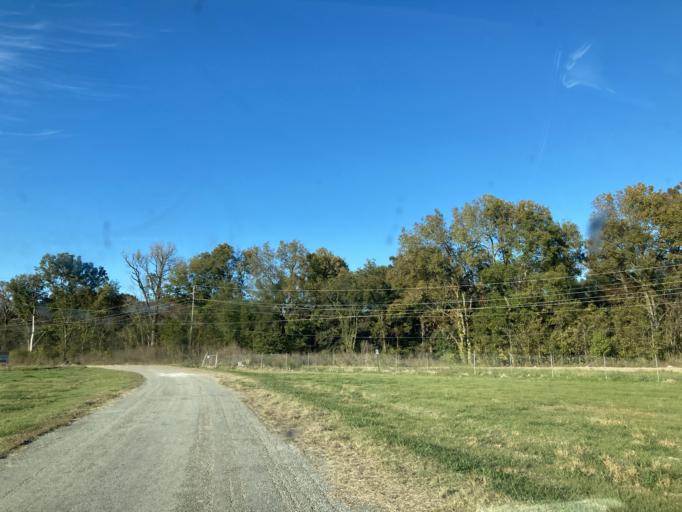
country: US
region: Mississippi
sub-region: Yazoo County
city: Yazoo City
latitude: 32.8824
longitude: -90.4203
